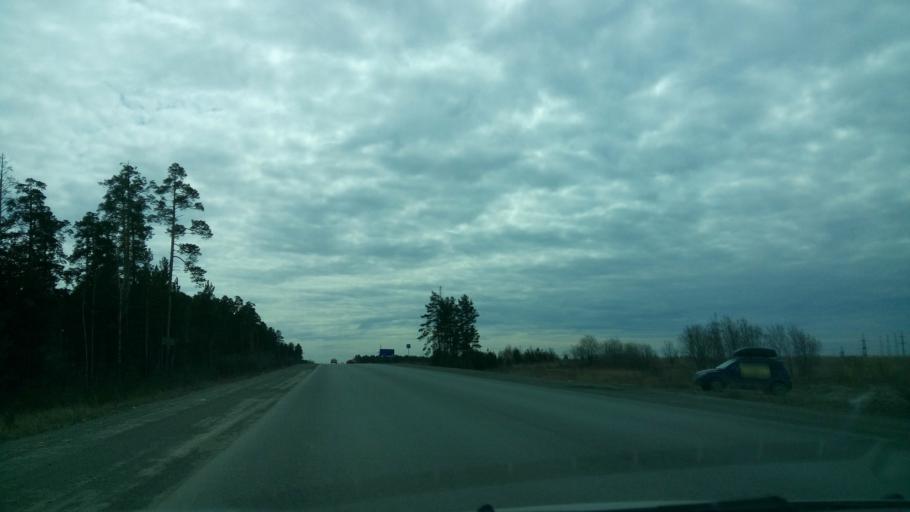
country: RU
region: Sverdlovsk
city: Verkhnyaya Pyshma
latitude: 56.9484
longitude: 60.6285
